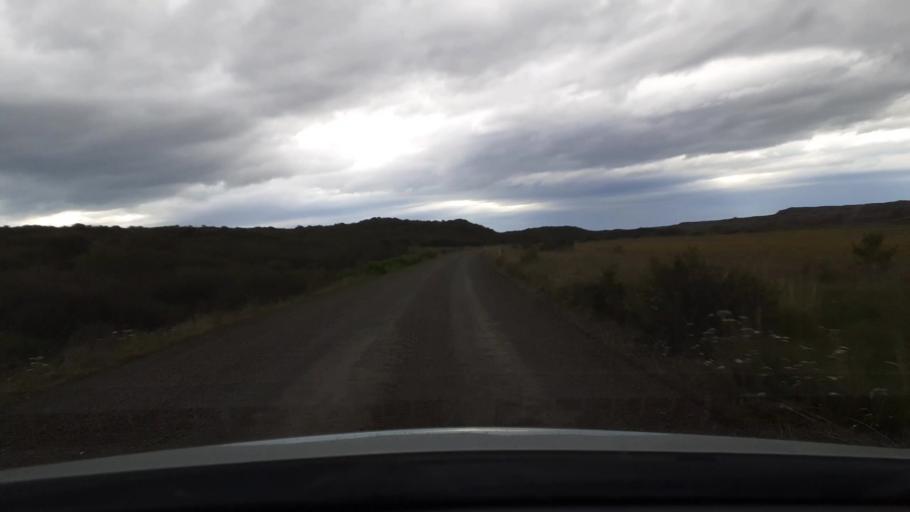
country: IS
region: West
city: Borgarnes
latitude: 64.6102
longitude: -21.9549
